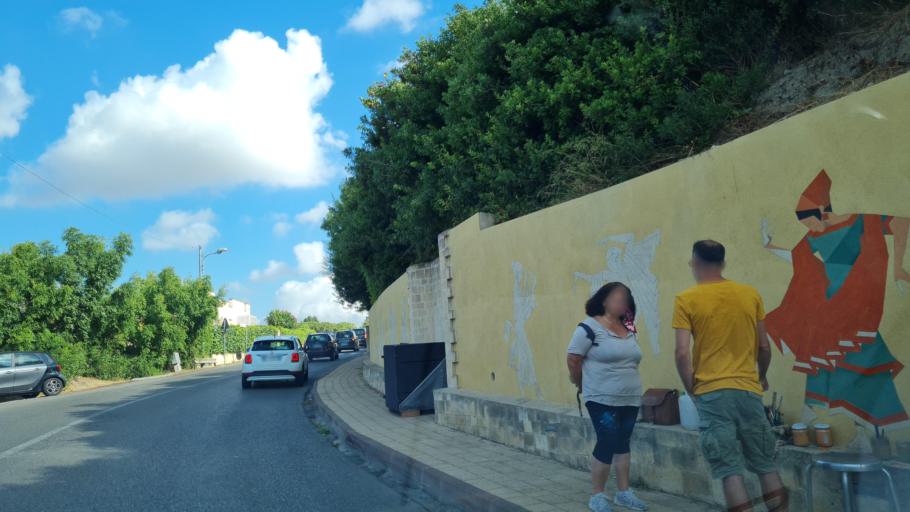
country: IT
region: Latium
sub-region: Provincia di Viterbo
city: Tarquinia
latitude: 42.2515
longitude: 11.7529
